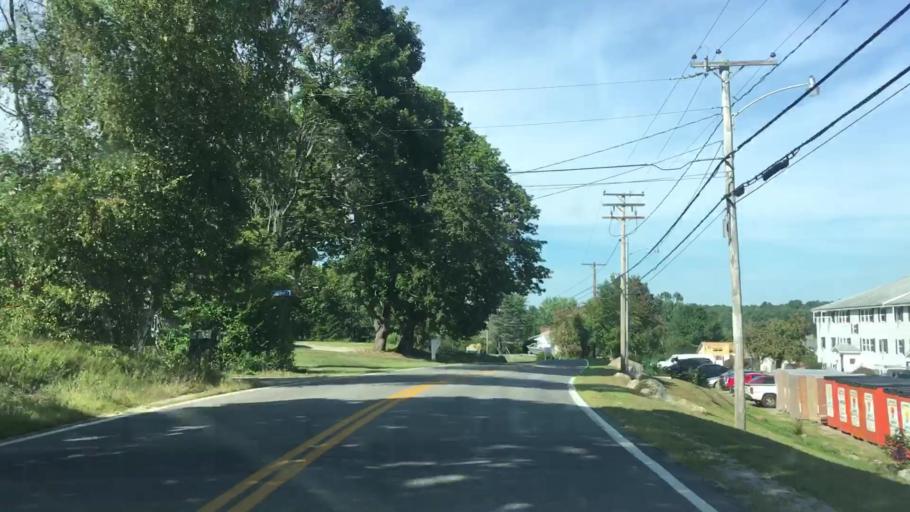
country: US
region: Maine
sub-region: Sagadahoc County
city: Bath
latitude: 43.9253
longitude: -69.8589
